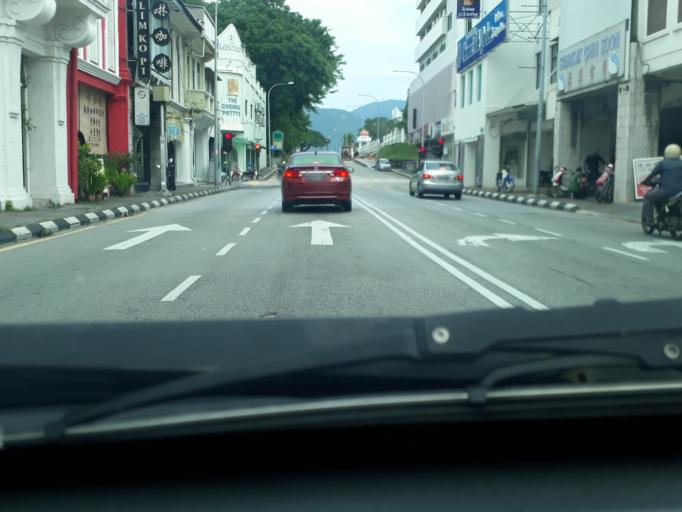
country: MY
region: Perak
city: Ipoh
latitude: 4.5951
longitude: 101.0774
